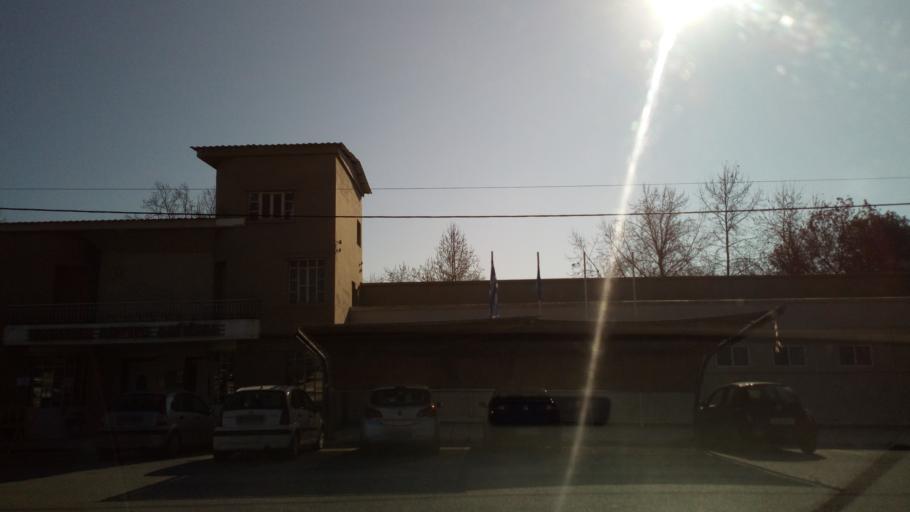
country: GR
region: Central Macedonia
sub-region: Nomos Thessalonikis
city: Lagkadas
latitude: 40.7336
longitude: 23.0849
